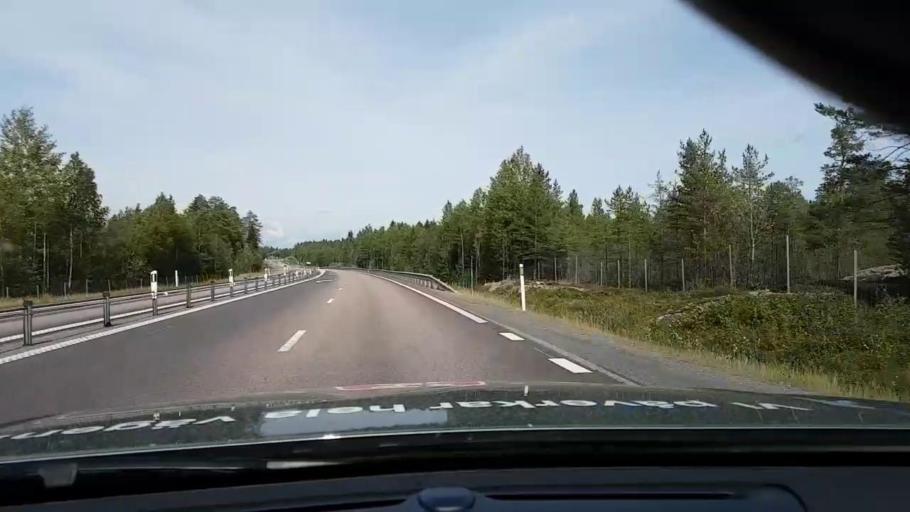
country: SE
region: Vaesternorrland
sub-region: OErnskoeldsviks Kommun
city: Husum
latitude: 63.3707
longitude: 19.1890
